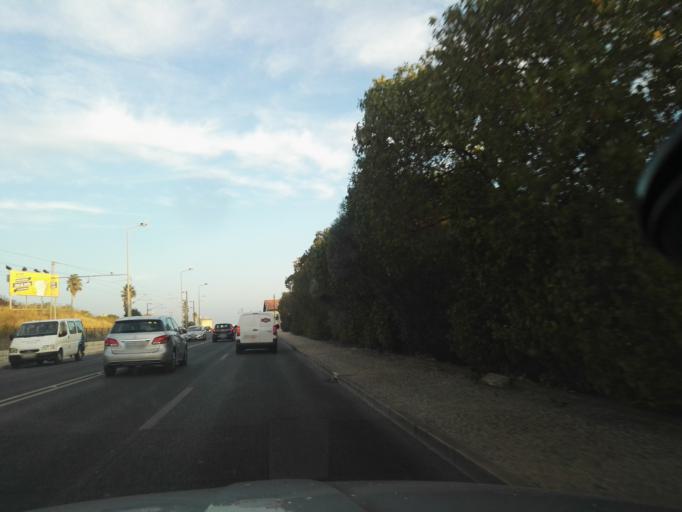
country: PT
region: Lisbon
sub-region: Cascais
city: Estoril
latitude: 38.6981
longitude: -9.3823
